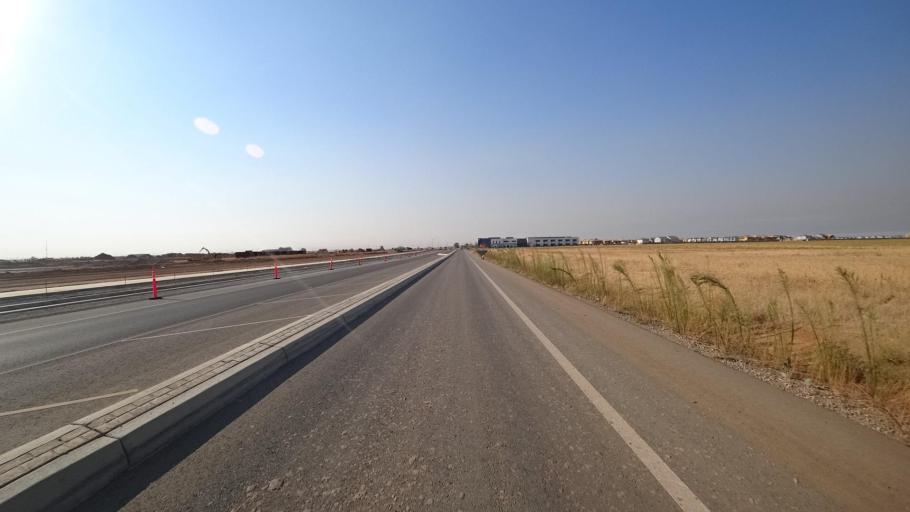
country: US
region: California
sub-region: Sacramento County
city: Elk Grove
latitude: 38.3830
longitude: -121.3992
